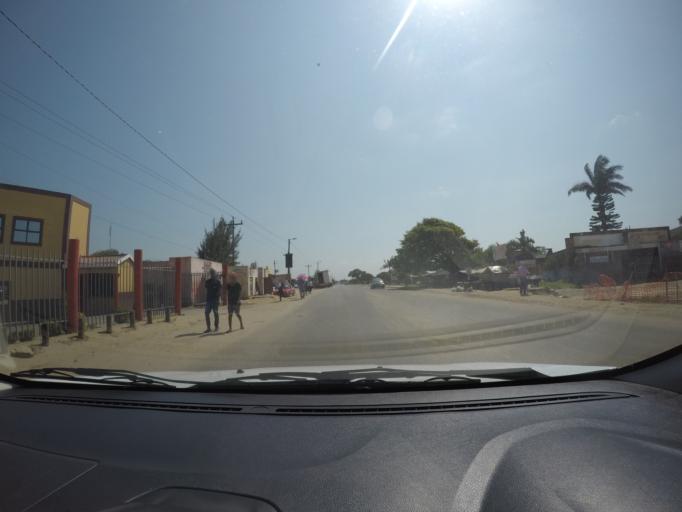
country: ZA
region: KwaZulu-Natal
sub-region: uThungulu District Municipality
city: eSikhawini
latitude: -28.8708
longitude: 31.9010
